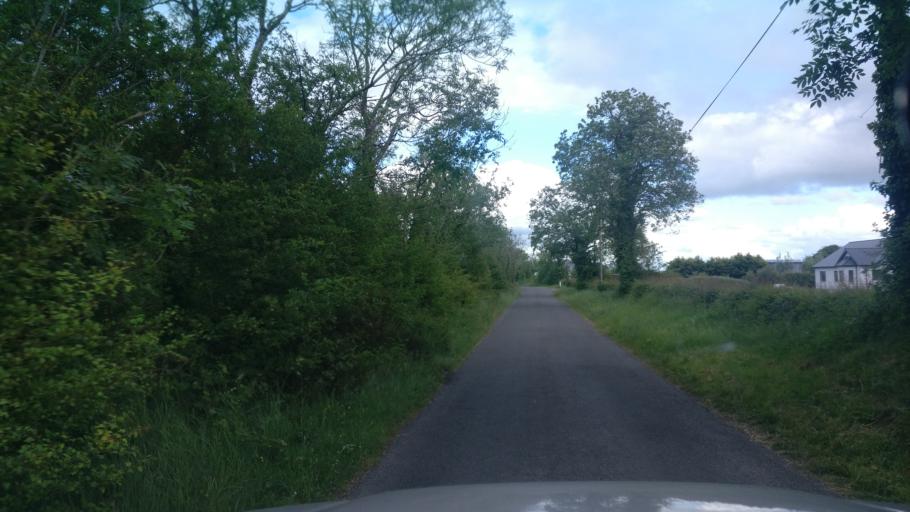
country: IE
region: Connaught
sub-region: County Galway
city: Portumna
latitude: 53.1992
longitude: -8.3304
